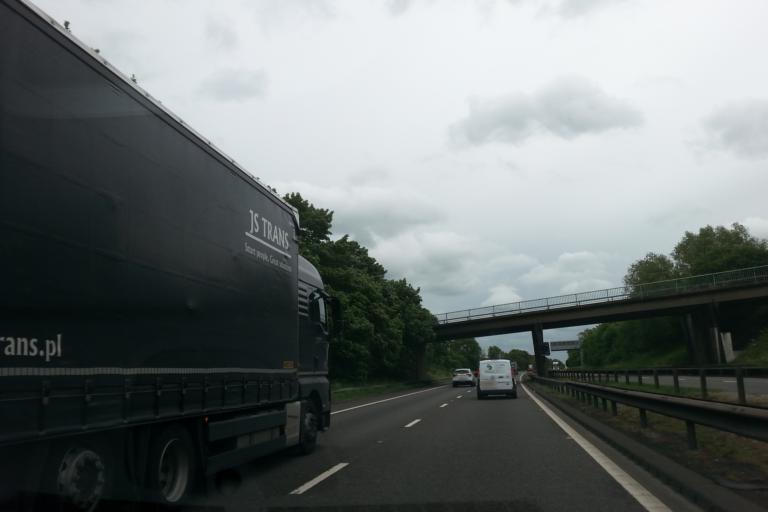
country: GB
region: England
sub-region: Doncaster
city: Tickhill
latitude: 53.4678
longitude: -1.1344
